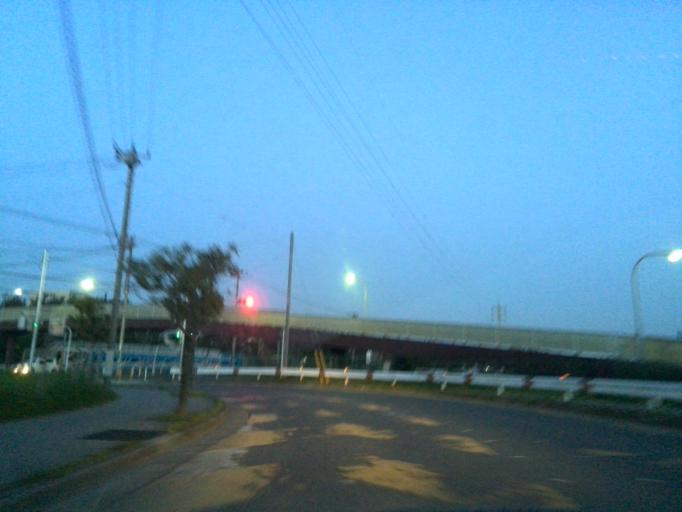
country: JP
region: Chiba
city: Funabashi
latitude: 35.6622
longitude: 140.0105
